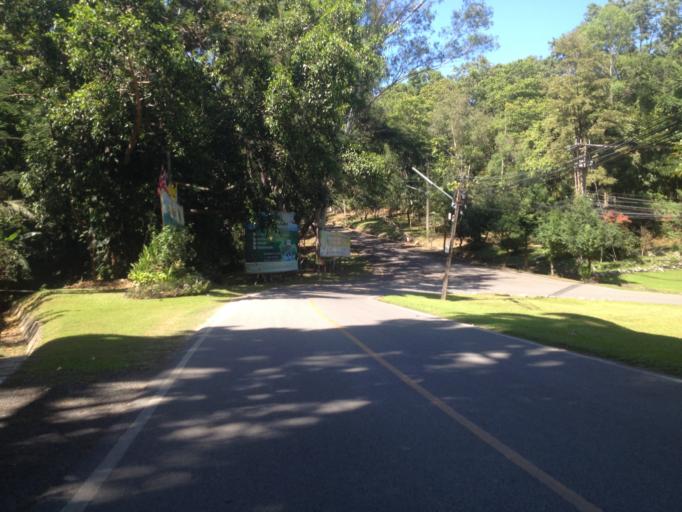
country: TH
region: Chiang Mai
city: Chiang Mai
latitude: 18.7945
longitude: 98.9465
